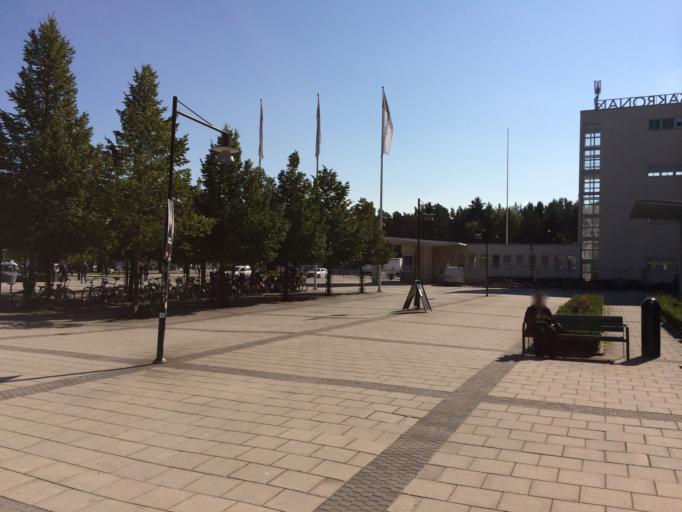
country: SE
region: Stockholm
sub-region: Stockholms Kommun
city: Arsta
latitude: 59.2990
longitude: 17.9947
